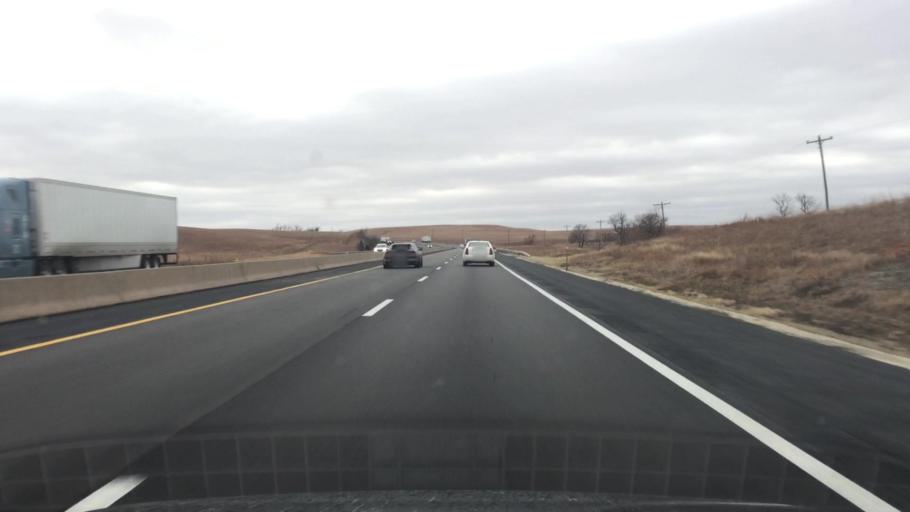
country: US
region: Kansas
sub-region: Chase County
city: Cottonwood Falls
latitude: 38.1211
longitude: -96.5597
